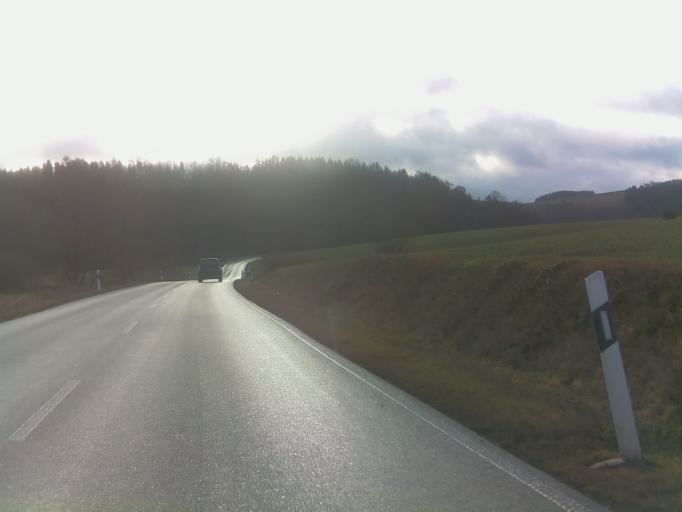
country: DE
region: Thuringia
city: Allendorf
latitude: 50.6649
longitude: 11.1519
